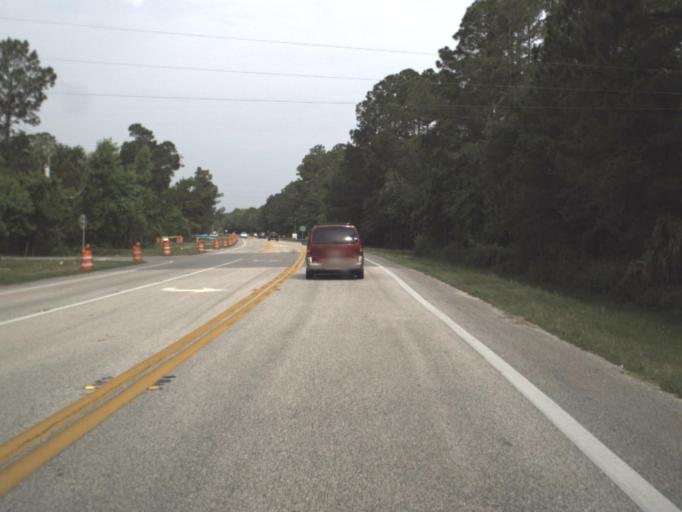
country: US
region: Florida
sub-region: Saint Johns County
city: Saint Augustine
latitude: 29.9582
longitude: -81.4635
